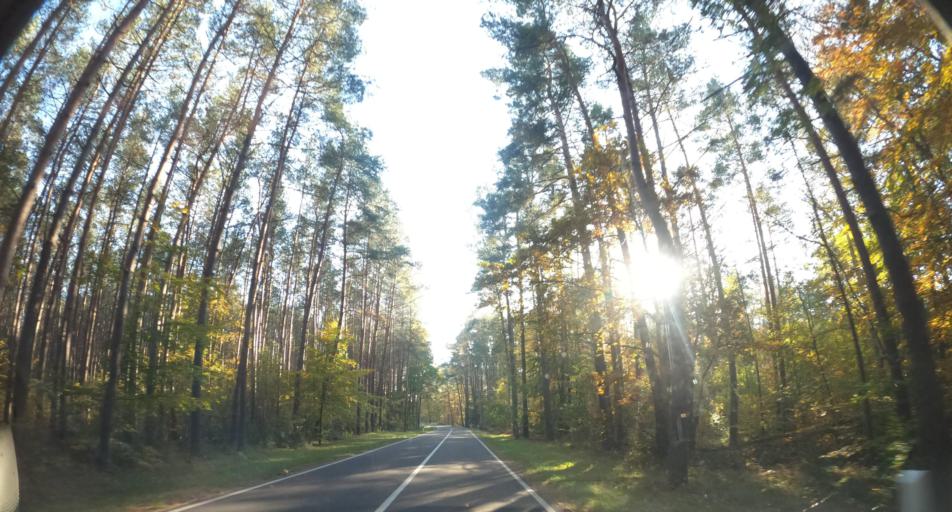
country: DE
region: Mecklenburg-Vorpommern
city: Ahlbeck
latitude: 53.6619
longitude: 14.1821
